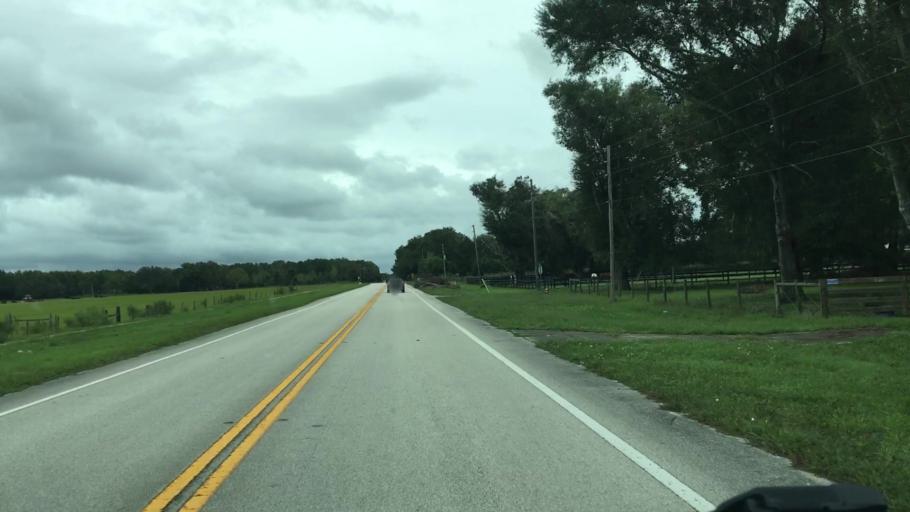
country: US
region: Florida
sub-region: Volusia County
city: Lake Helen
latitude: 28.9806
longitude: -81.2235
